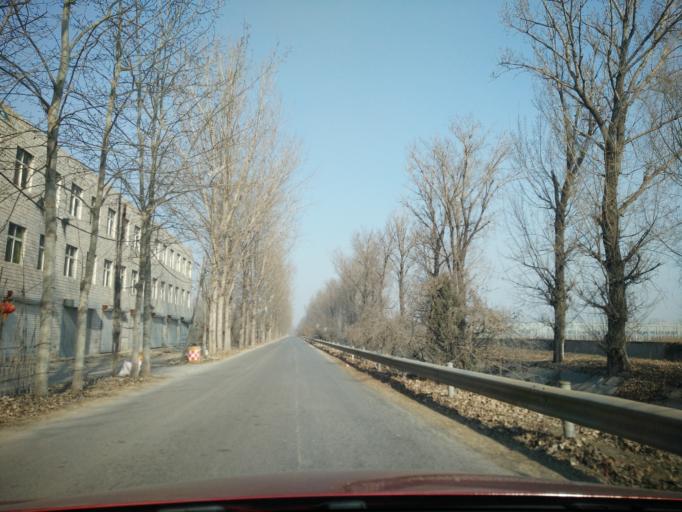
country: CN
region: Beijing
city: Yinghai
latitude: 39.7091
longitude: 116.4472
